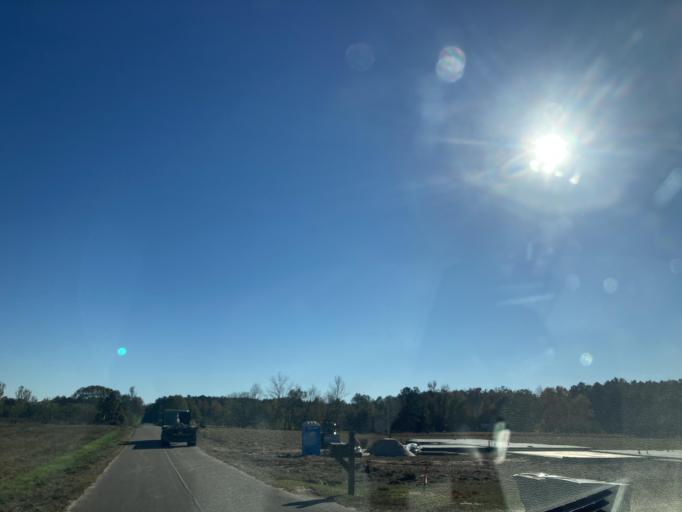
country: US
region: Mississippi
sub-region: Lamar County
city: Sumrall
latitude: 31.3866
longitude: -89.6075
